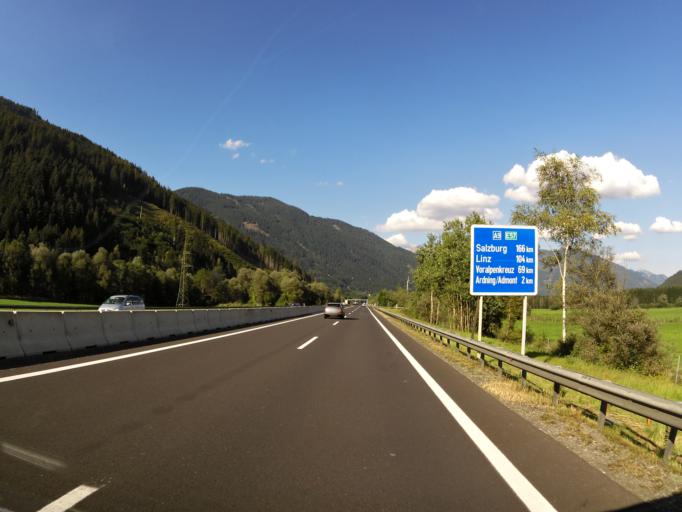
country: AT
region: Styria
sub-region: Politischer Bezirk Liezen
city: Selzthal
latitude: 47.5609
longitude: 14.3044
